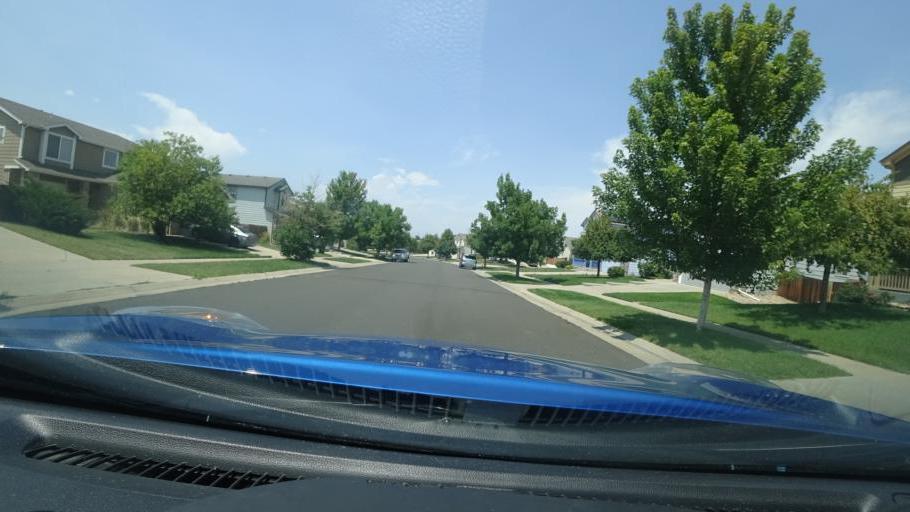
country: US
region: Colorado
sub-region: Adams County
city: Aurora
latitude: 39.6752
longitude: -104.7679
